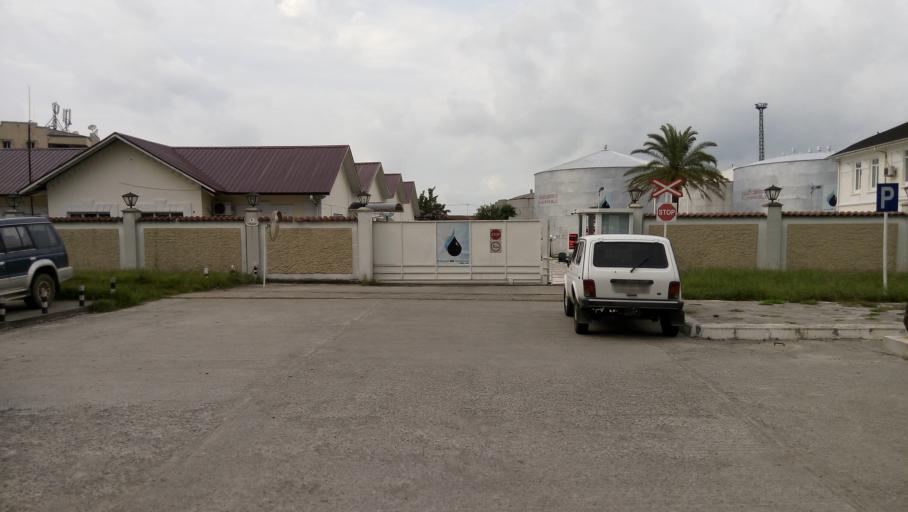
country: GE
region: Ajaria
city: Batumi
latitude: 41.6428
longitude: 41.6572
